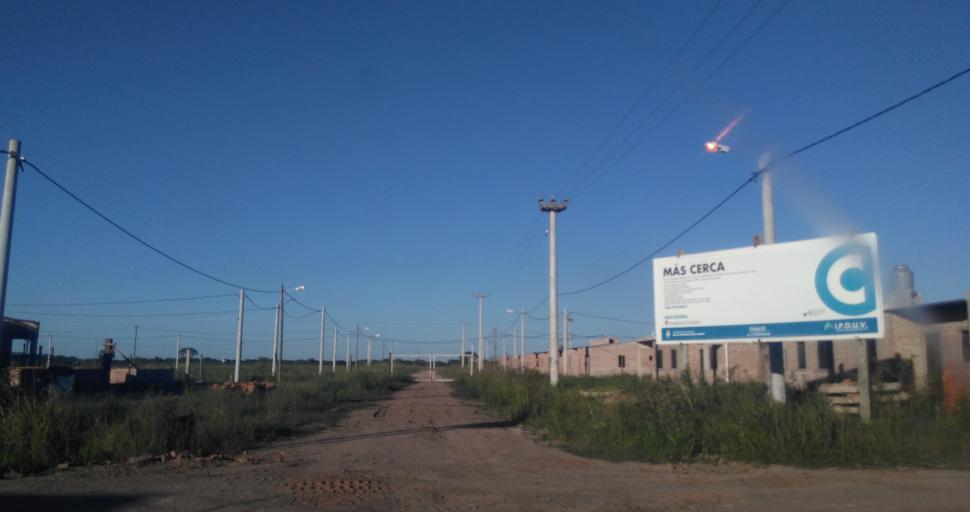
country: AR
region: Chaco
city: Fontana
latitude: -27.3969
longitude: -58.9870
